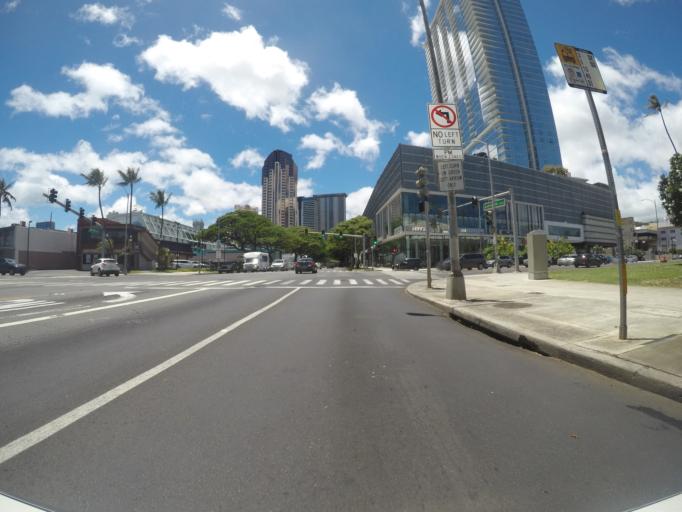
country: US
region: Hawaii
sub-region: Honolulu County
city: Honolulu
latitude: 21.2988
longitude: -157.8525
